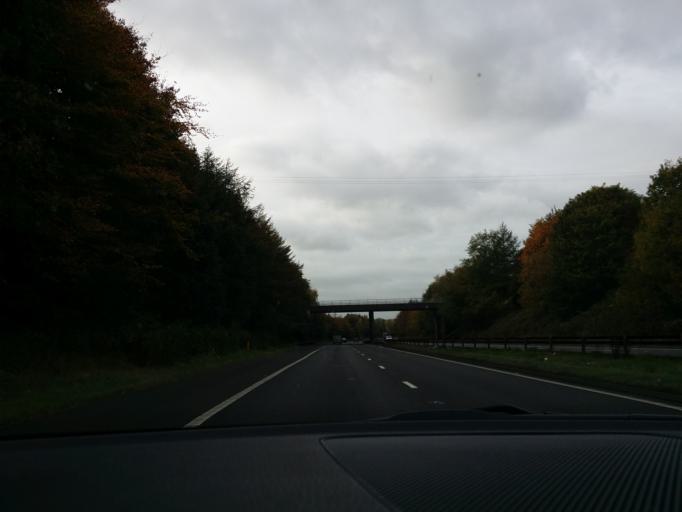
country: GB
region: Scotland
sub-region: West Lothian
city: Linlithgow
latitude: 55.9812
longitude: -3.6118
